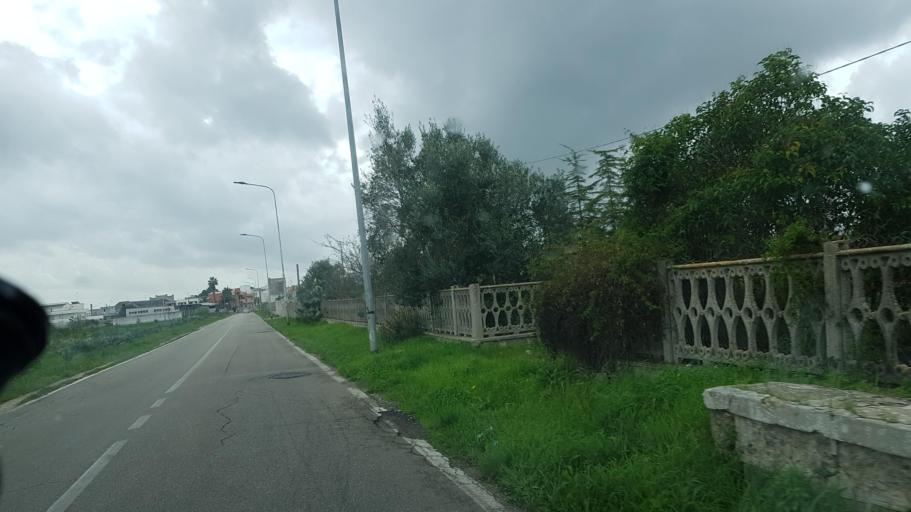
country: IT
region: Apulia
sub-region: Provincia di Lecce
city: Carmiano
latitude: 40.3539
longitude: 18.0457
